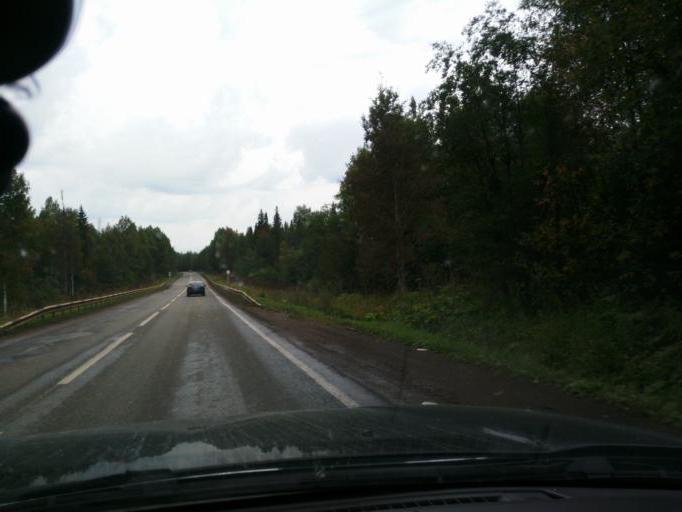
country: RU
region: Perm
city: Chernushka
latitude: 56.6978
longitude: 56.1825
